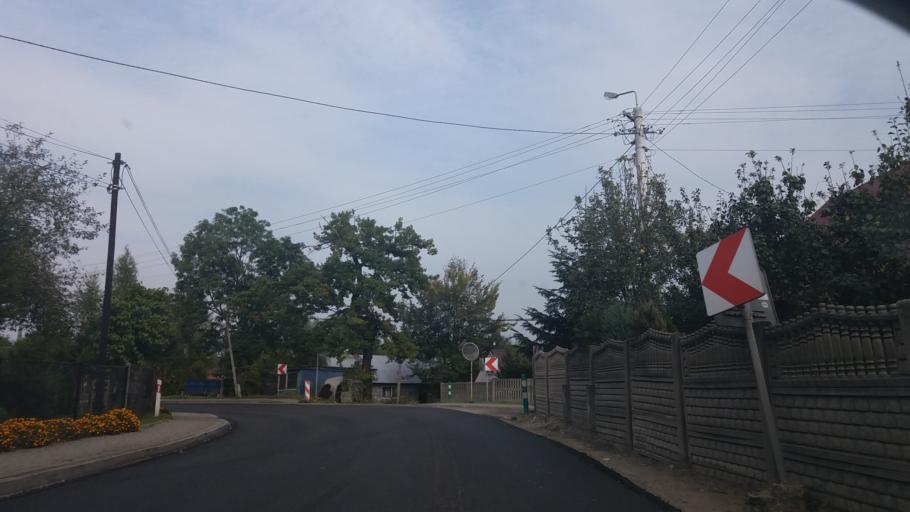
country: PL
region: Lesser Poland Voivodeship
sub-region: Powiat chrzanowski
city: Babice
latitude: 50.0387
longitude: 19.4413
